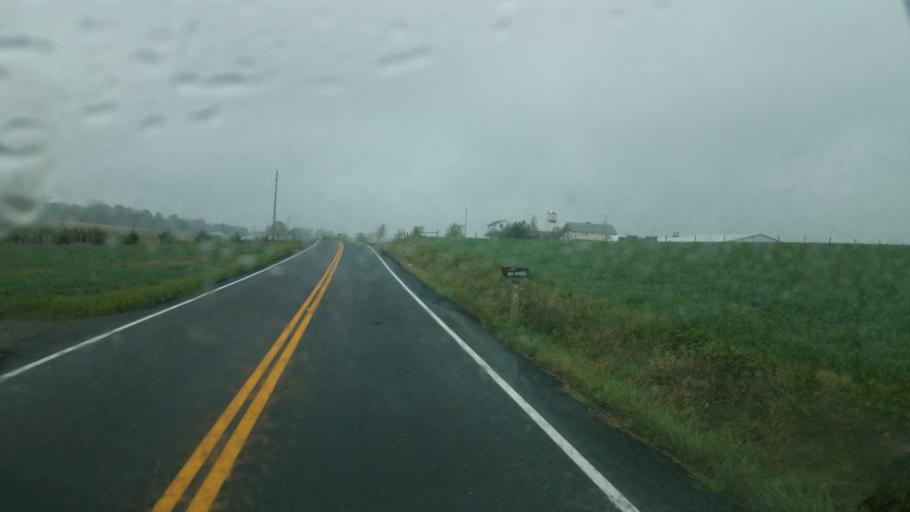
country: US
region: Ohio
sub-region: Wayne County
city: Shreve
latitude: 40.6125
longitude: -82.0599
